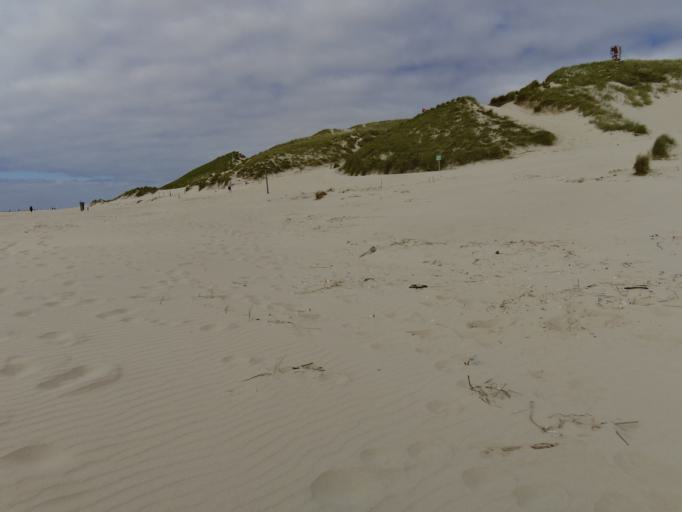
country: DE
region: Schleswig-Holstein
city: Nebel
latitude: 54.6254
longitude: 8.3520
